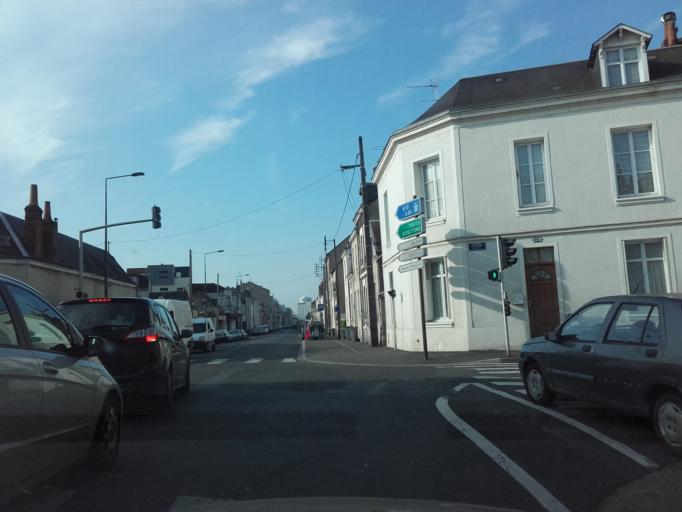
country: FR
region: Centre
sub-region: Departement d'Indre-et-Loire
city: Tours
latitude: 47.3828
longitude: 0.6771
